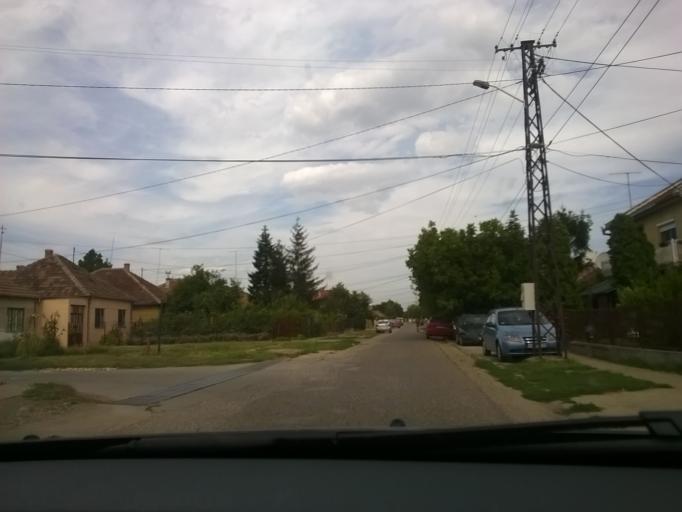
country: RS
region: Autonomna Pokrajina Vojvodina
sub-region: Juznobanatski Okrug
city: Vrsac
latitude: 45.1191
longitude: 21.2828
